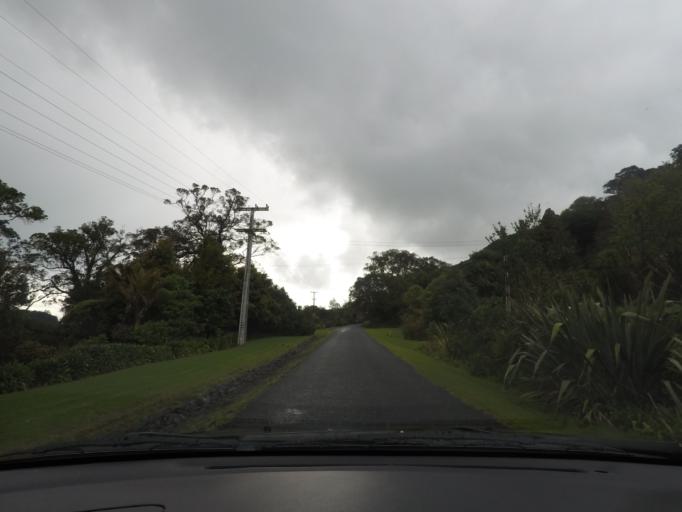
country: NZ
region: Auckland
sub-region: Auckland
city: Warkworth
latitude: -36.4747
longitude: 174.7357
